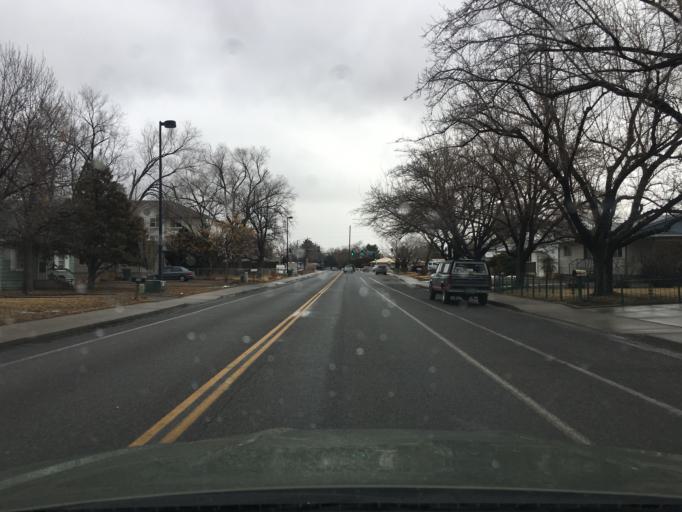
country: US
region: Colorado
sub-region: Mesa County
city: Grand Junction
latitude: 39.0810
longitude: -108.5730
